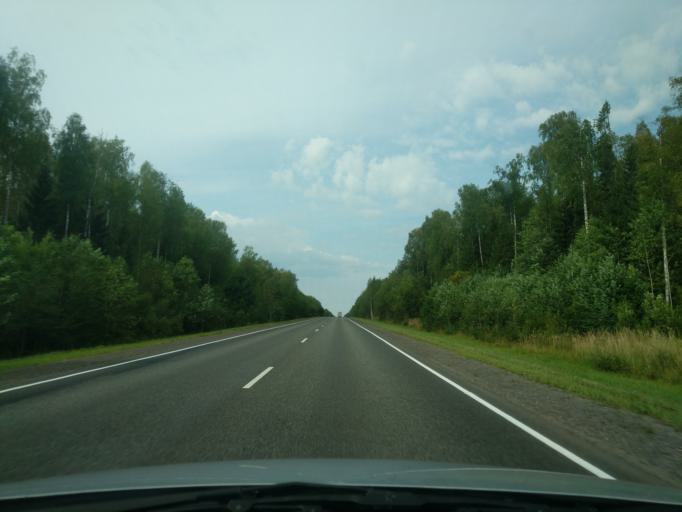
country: RU
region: Kirov
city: Leninskoye
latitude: 58.3187
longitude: 46.8929
